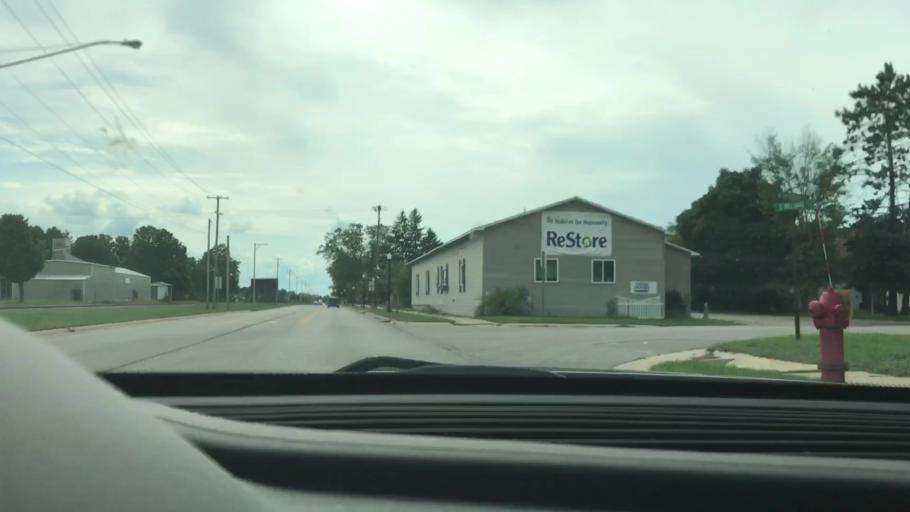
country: US
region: Michigan
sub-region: Antrim County
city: Mancelona
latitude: 44.9009
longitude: -85.0622
